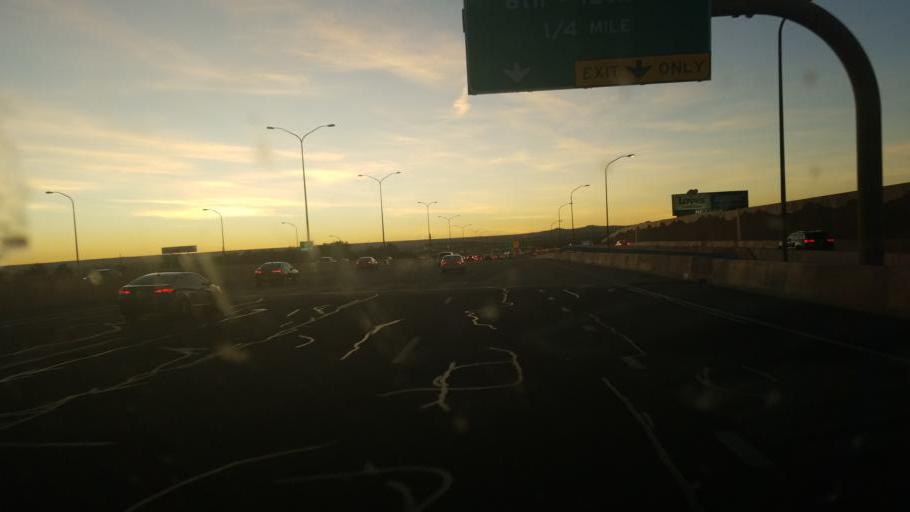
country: US
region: New Mexico
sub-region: Bernalillo County
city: Albuquerque
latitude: 35.1055
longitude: -106.6414
